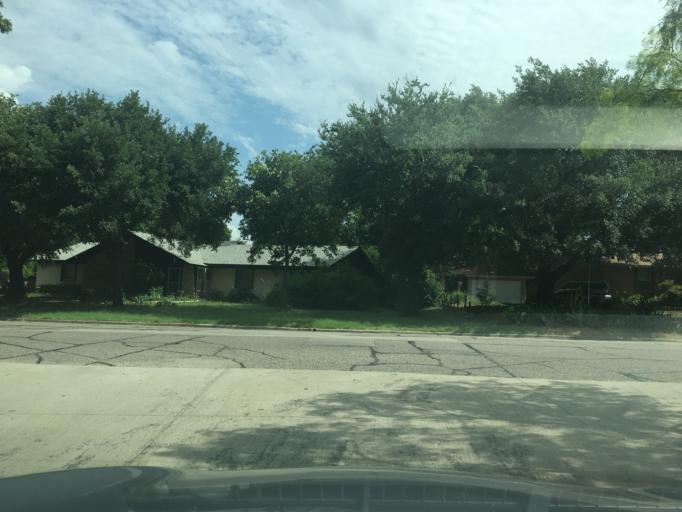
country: US
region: Texas
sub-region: Dallas County
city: Carrollton
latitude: 32.9390
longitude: -96.8595
